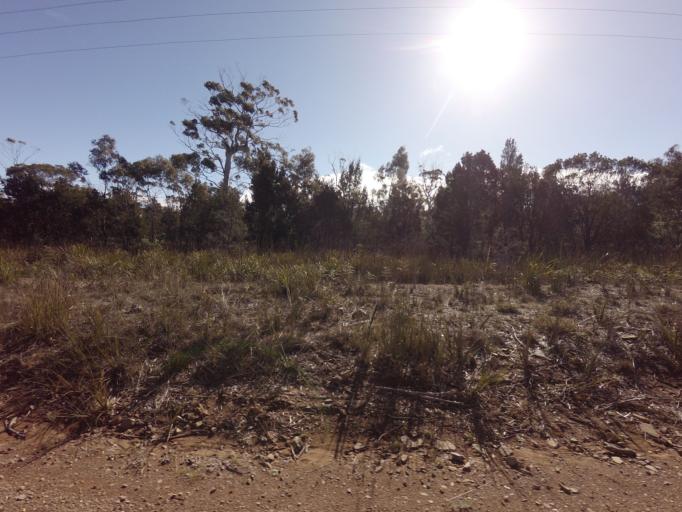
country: AU
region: Tasmania
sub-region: Sorell
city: Sorell
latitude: -42.3544
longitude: 147.9670
